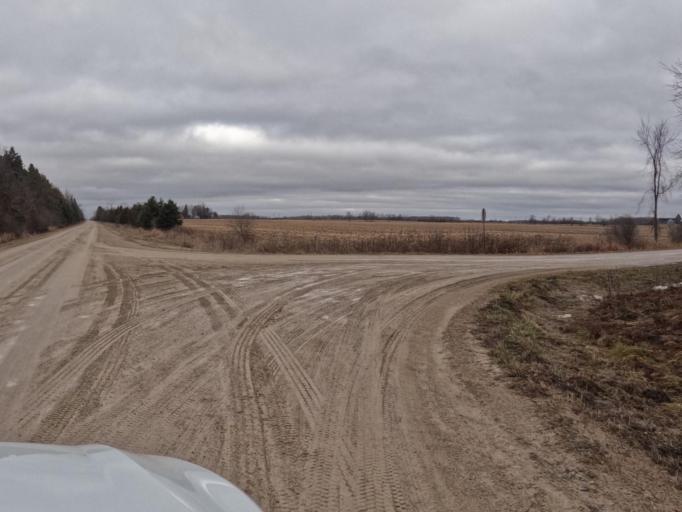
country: CA
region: Ontario
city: Shelburne
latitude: 43.9577
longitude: -80.3984
